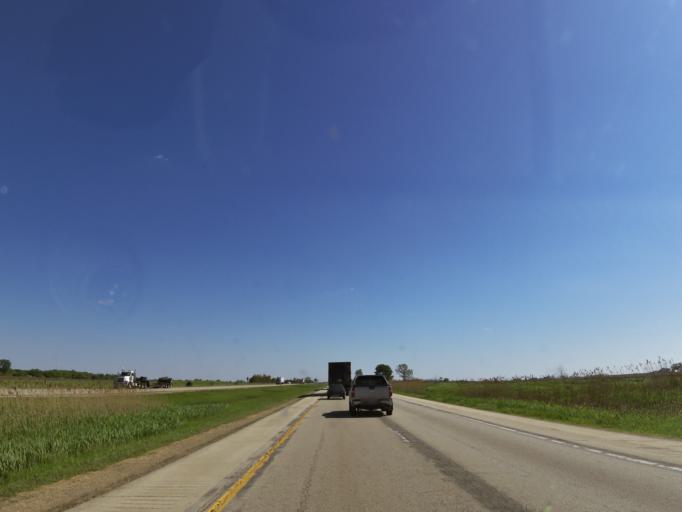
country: US
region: Illinois
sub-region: Ogle County
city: Davis Junction
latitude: 42.0396
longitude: -89.0212
